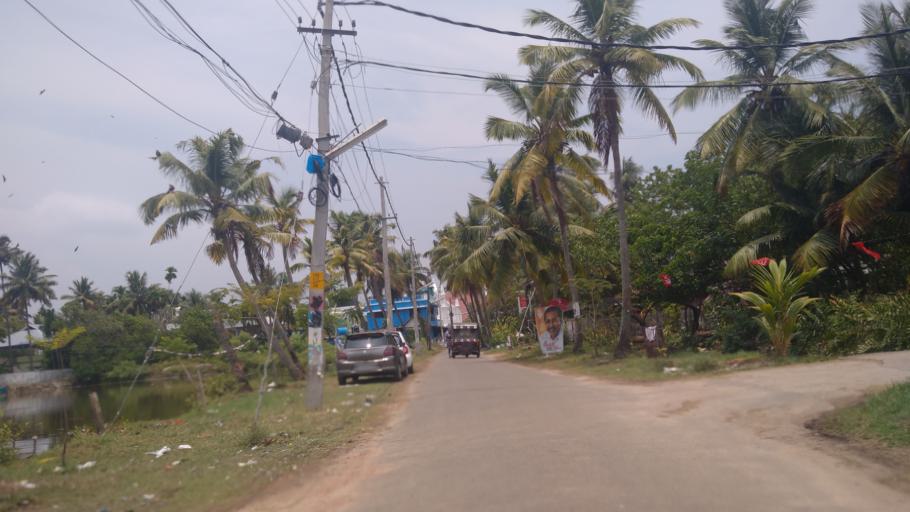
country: IN
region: Kerala
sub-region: Ernakulam
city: Cochin
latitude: 9.9999
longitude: 76.2380
